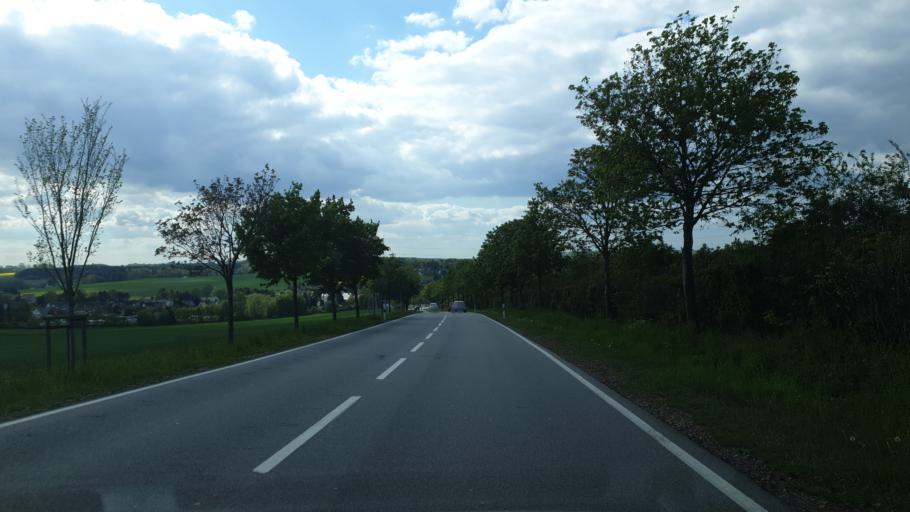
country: DE
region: Saxony
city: Lugau
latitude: 50.7045
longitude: 12.7461
